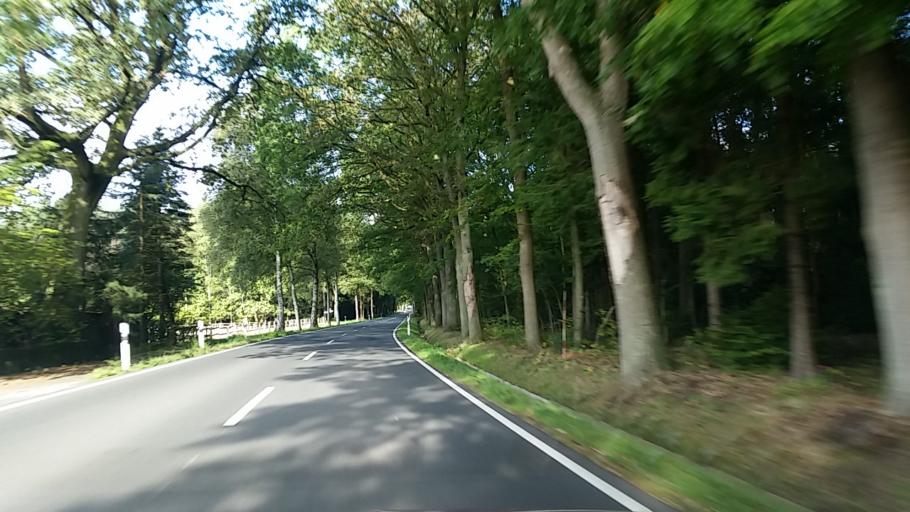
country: DE
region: Lower Saxony
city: Bad Fallingbostel
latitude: 52.9091
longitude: 9.7261
